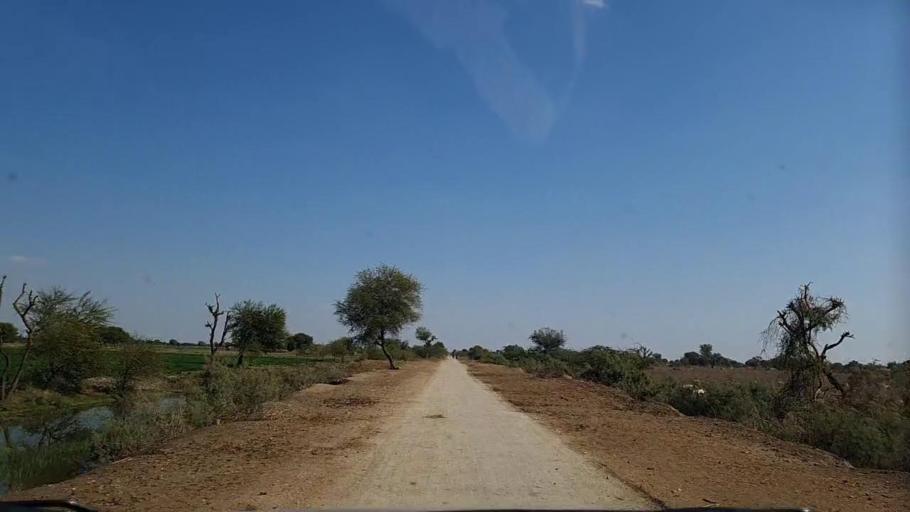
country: PK
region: Sindh
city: Pithoro
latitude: 25.6864
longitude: 69.4510
